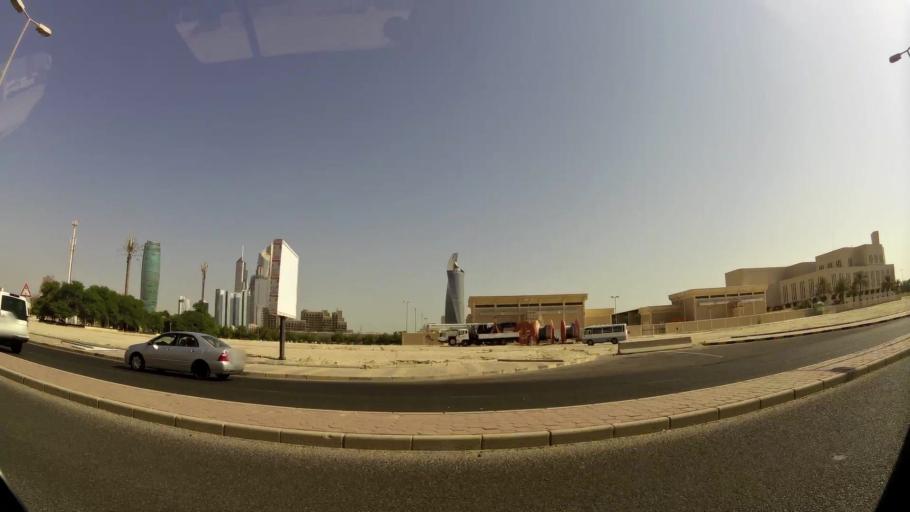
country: KW
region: Al Asimah
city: Kuwait City
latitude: 29.3646
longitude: 47.9840
